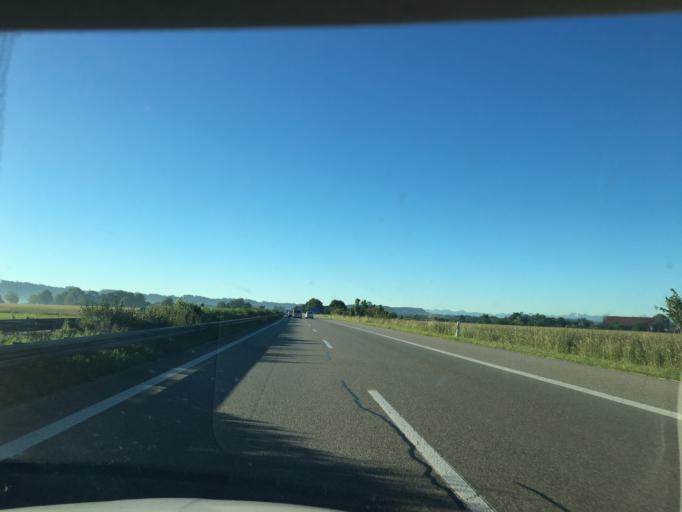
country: DE
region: Bavaria
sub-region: Swabia
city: Woringen
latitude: 47.9230
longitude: 10.2172
